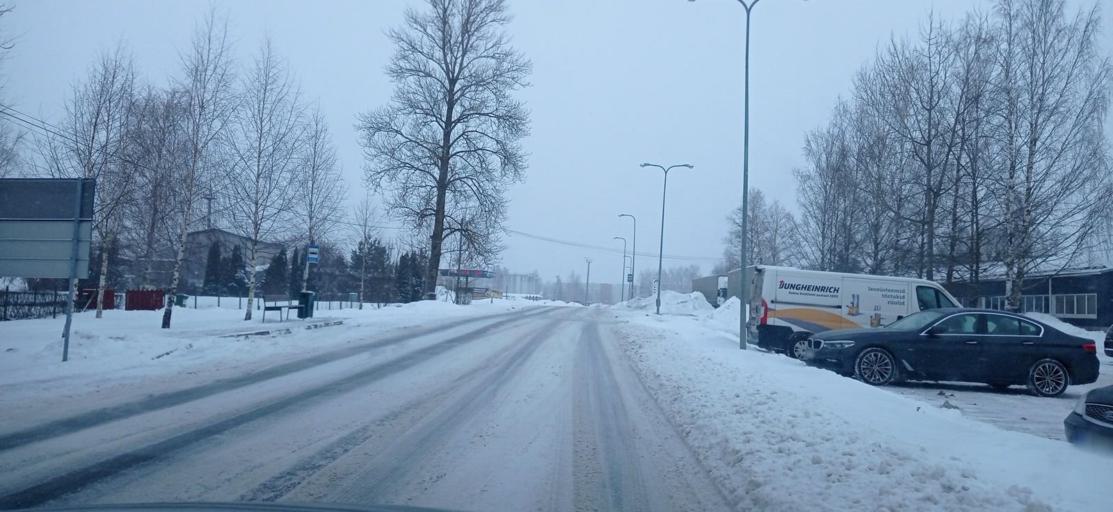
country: EE
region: Viljandimaa
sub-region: Viljandi linn
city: Viljandi
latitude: 58.3532
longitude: 25.5729
